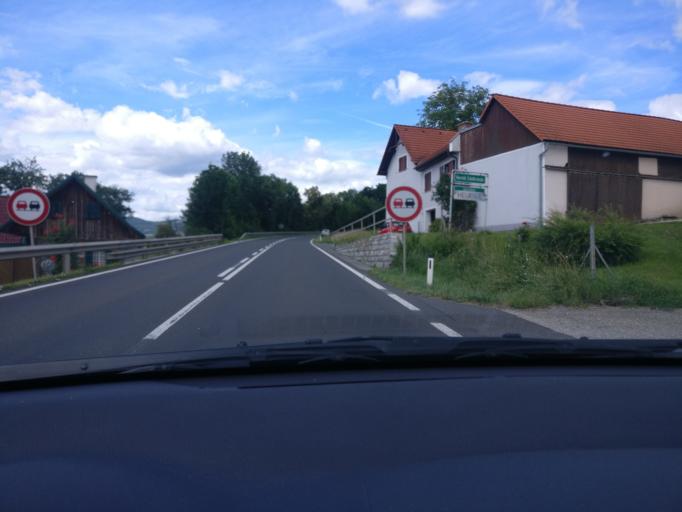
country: AT
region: Styria
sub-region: Politischer Bezirk Hartberg-Fuerstenfeld
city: Kaibing
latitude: 47.2028
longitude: 15.8417
